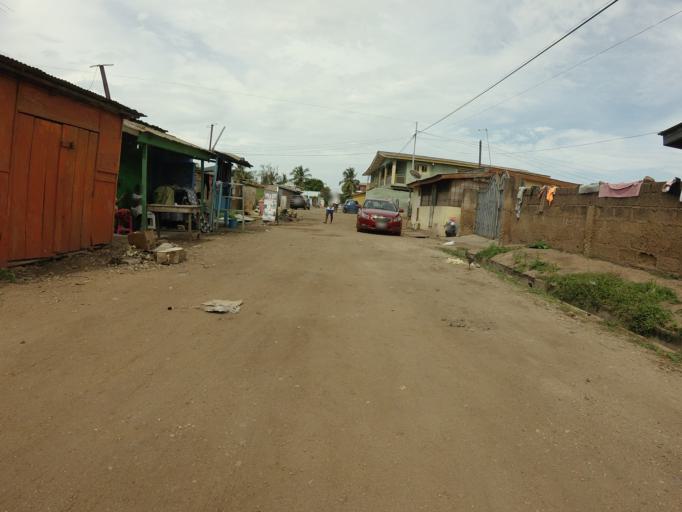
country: GH
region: Greater Accra
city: Accra
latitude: 5.5979
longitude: -0.2149
